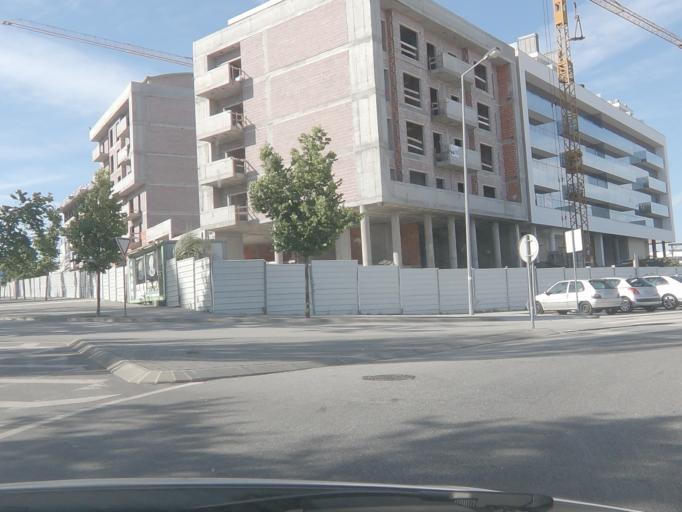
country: PT
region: Viseu
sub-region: Viseu
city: Viseu
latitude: 40.6445
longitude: -7.9098
